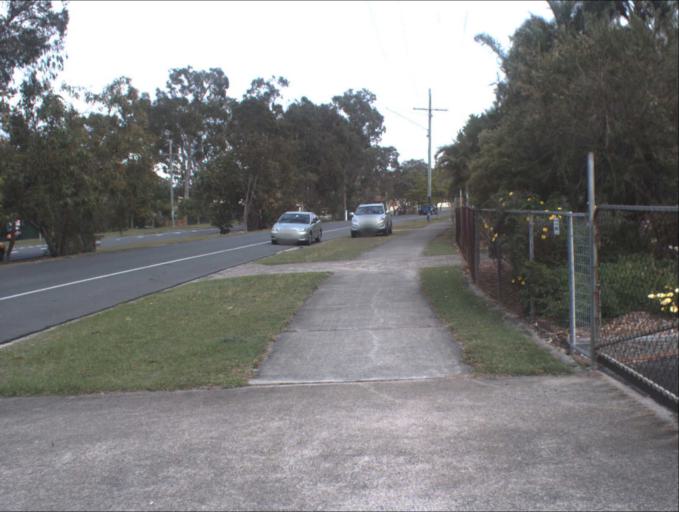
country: AU
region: Queensland
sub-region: Logan
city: Logan Reserve
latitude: -27.6790
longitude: 153.0670
